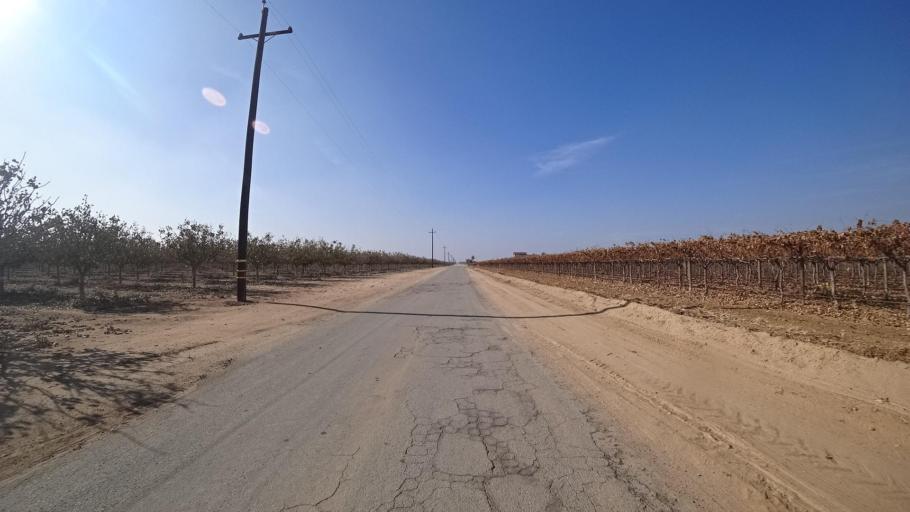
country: US
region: California
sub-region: Kern County
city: Shafter
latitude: 35.5442
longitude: -119.1445
